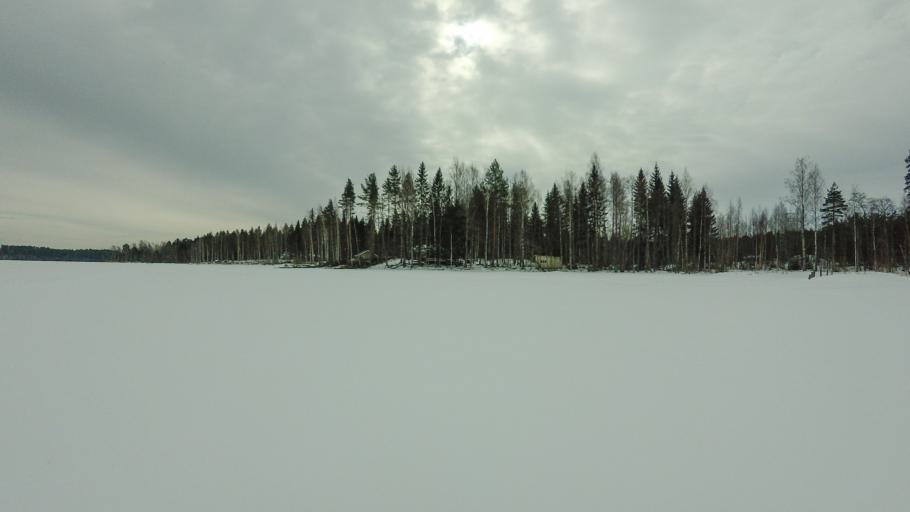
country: FI
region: Southern Savonia
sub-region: Savonlinna
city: Enonkoski
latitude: 62.1204
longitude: 28.6237
